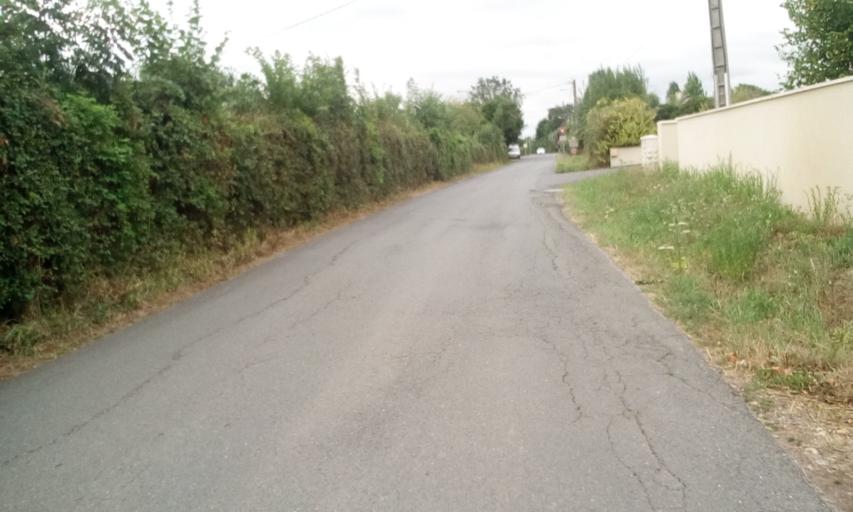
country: FR
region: Lower Normandy
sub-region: Departement du Calvados
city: Troarn
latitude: 49.1904
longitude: -0.1842
